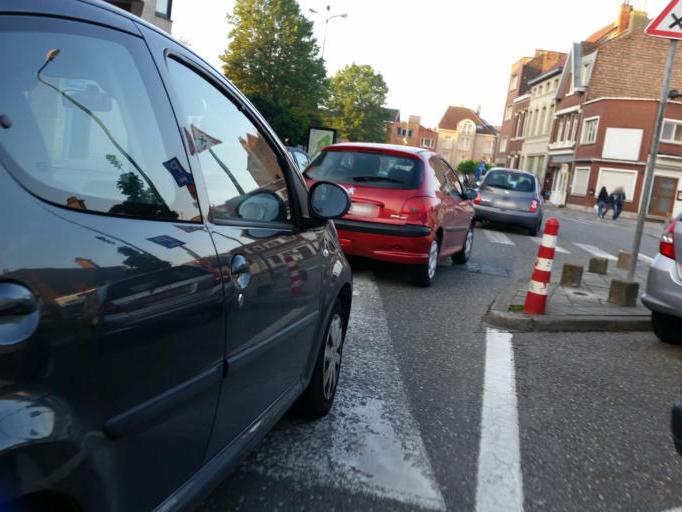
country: BE
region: Flanders
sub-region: Provincie Vlaams-Brabant
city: Vilvoorde
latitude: 50.9319
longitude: 4.4239
